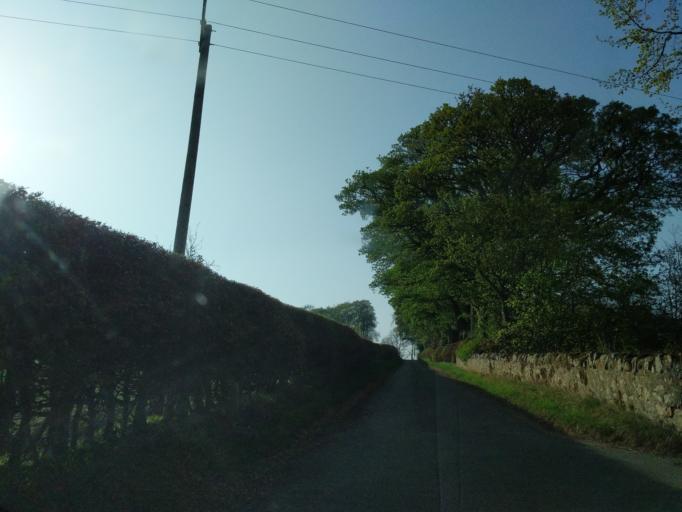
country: GB
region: Scotland
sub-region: Fife
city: Pathhead
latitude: 55.8581
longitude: -2.9281
